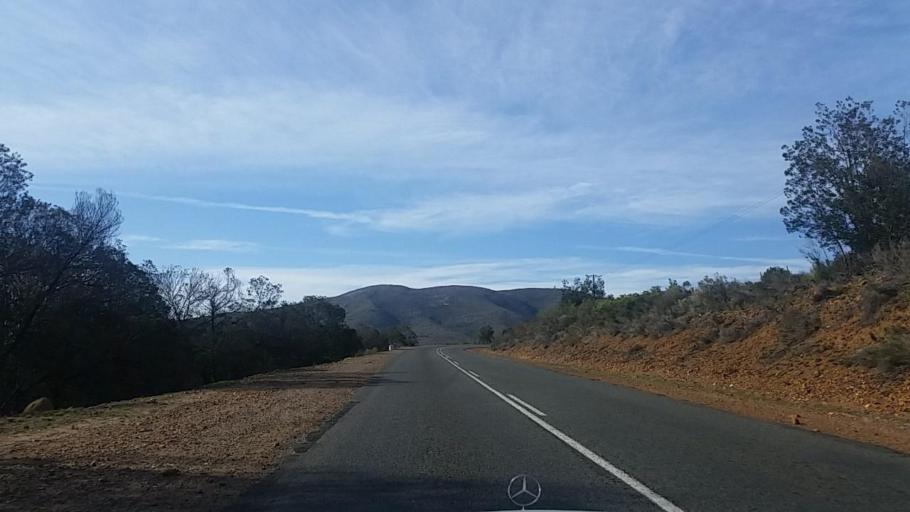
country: ZA
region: Western Cape
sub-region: Eden District Municipality
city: George
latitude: -33.8234
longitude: 22.3500
